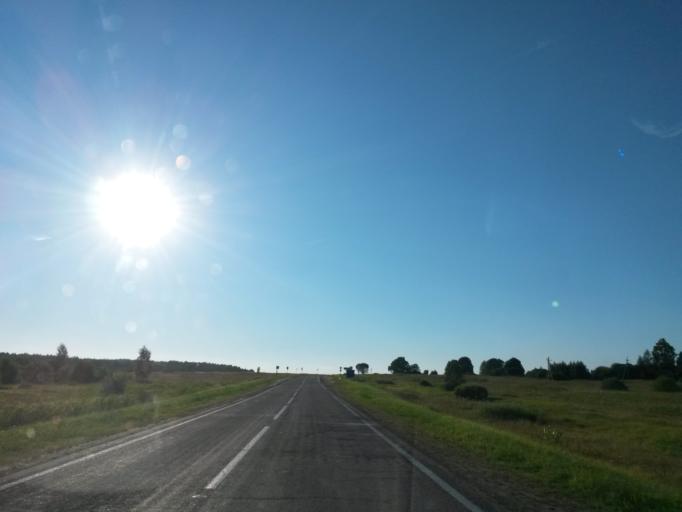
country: RU
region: Jaroslavl
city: Gavrilov-Yam
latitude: 57.2818
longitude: 39.9057
